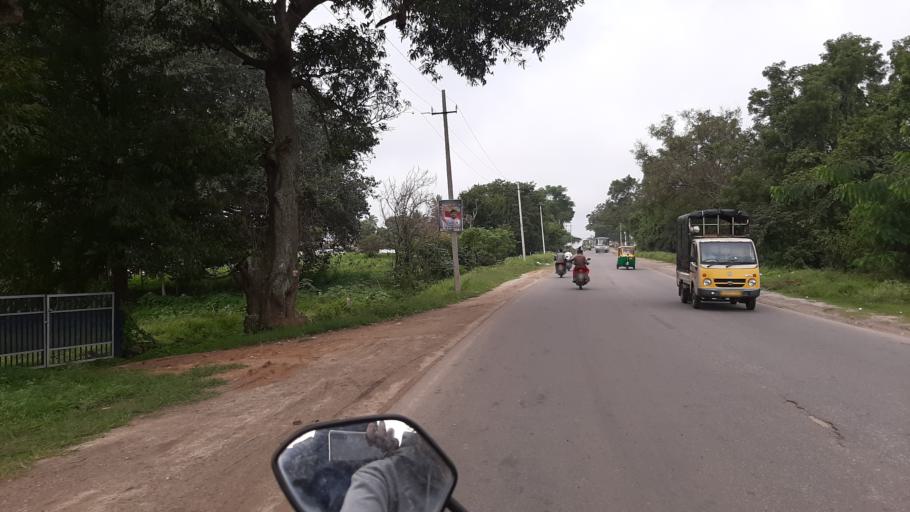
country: IN
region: Karnataka
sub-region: Bangalore Rural
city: Nelamangala
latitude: 12.9699
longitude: 77.4126
